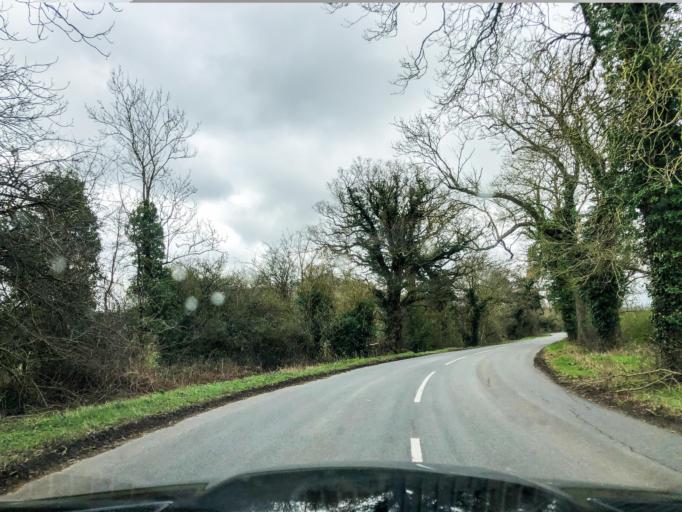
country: GB
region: England
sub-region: Oxfordshire
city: Hanwell
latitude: 52.1420
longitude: -1.4455
